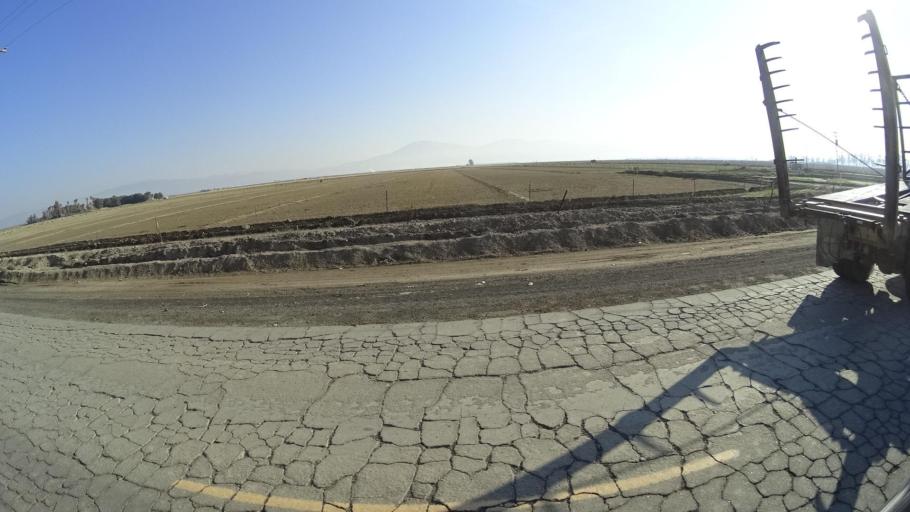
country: US
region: California
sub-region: Kern County
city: Weedpatch
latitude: 35.1947
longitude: -118.9678
